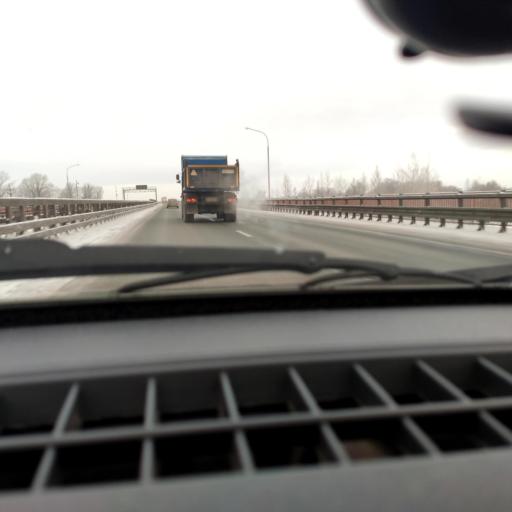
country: RU
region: Bashkortostan
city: Asanovo
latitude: 54.9716
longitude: 55.5768
